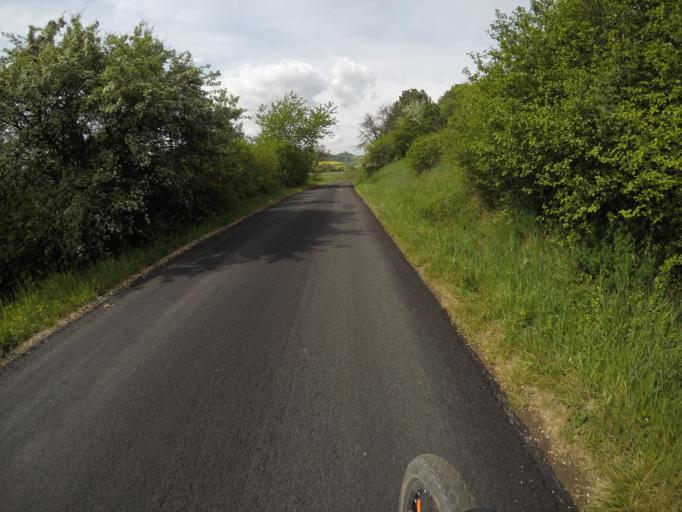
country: DE
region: Baden-Wuerttemberg
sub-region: Tuebingen Region
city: Tuebingen
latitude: 48.5263
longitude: 9.0064
